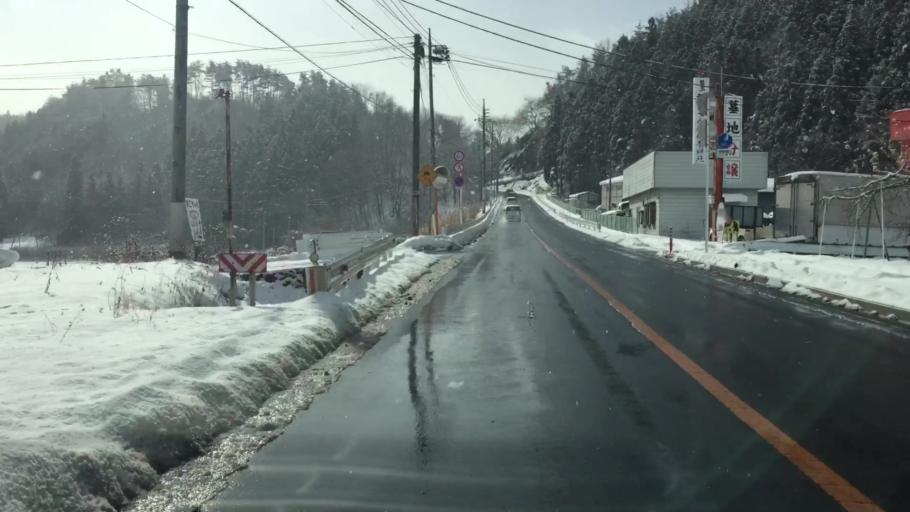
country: JP
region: Gunma
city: Numata
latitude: 36.6842
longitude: 139.0630
